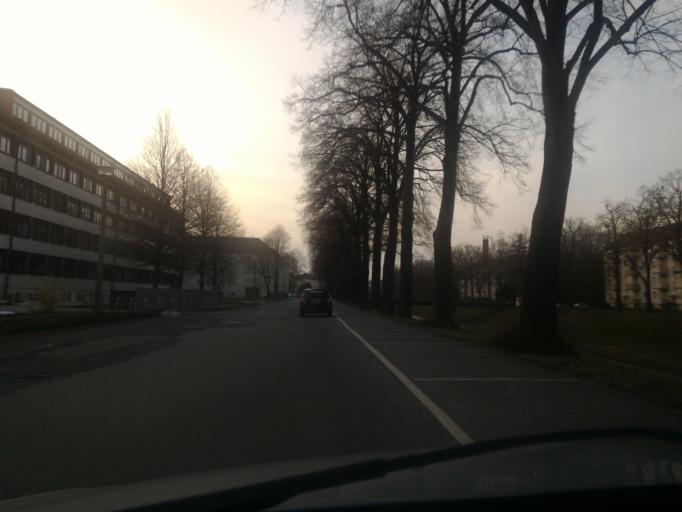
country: DE
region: Saxony
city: Zittau
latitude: 50.8912
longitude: 14.8039
